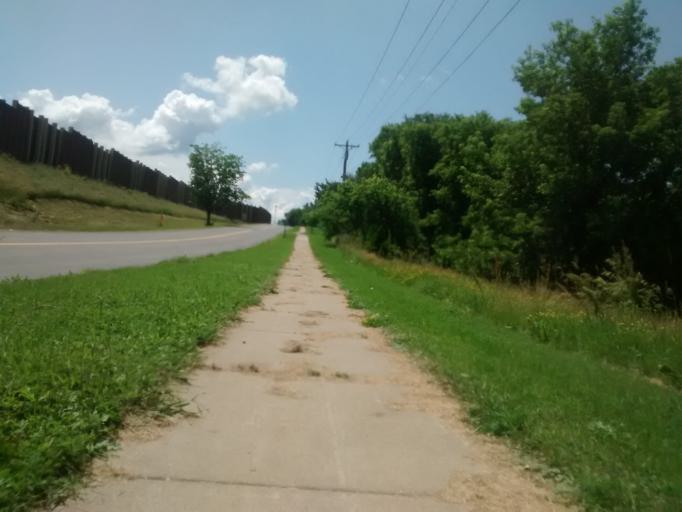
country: US
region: Minnesota
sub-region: Dakota County
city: Burnsville
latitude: 44.7637
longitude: -93.2896
